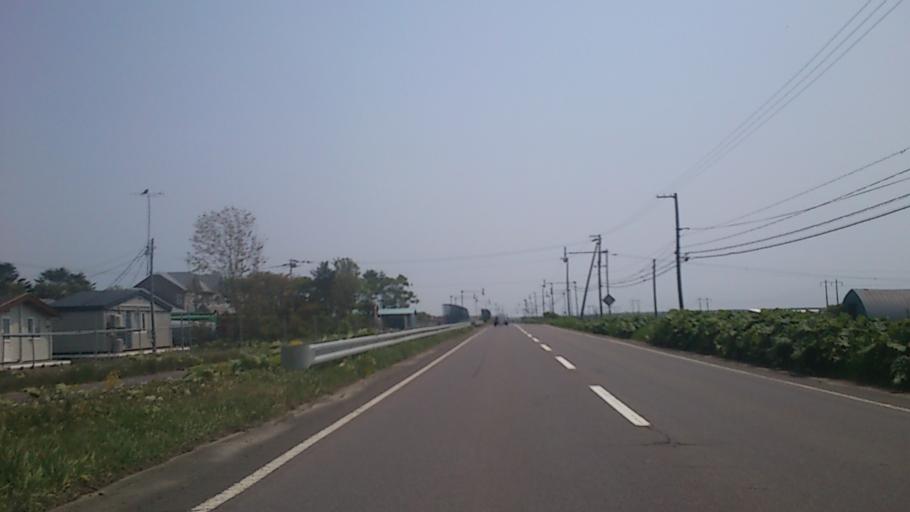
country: JP
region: Hokkaido
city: Nemuro
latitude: 43.2470
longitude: 145.2994
